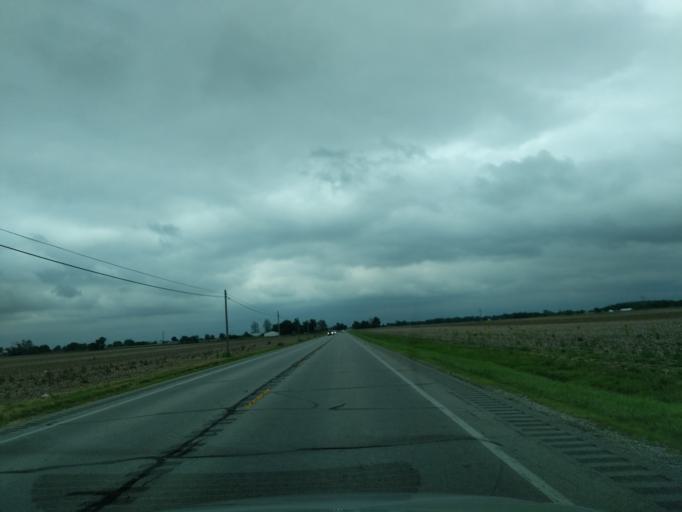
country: US
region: Indiana
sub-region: Madison County
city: Frankton
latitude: 40.2775
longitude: -85.7828
